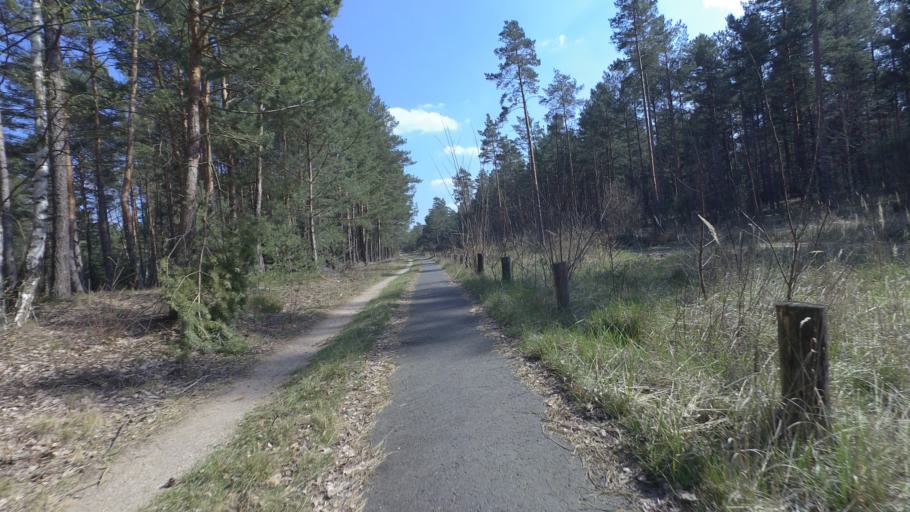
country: DE
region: Brandenburg
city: Mittenwalde
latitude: 52.1897
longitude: 13.5304
